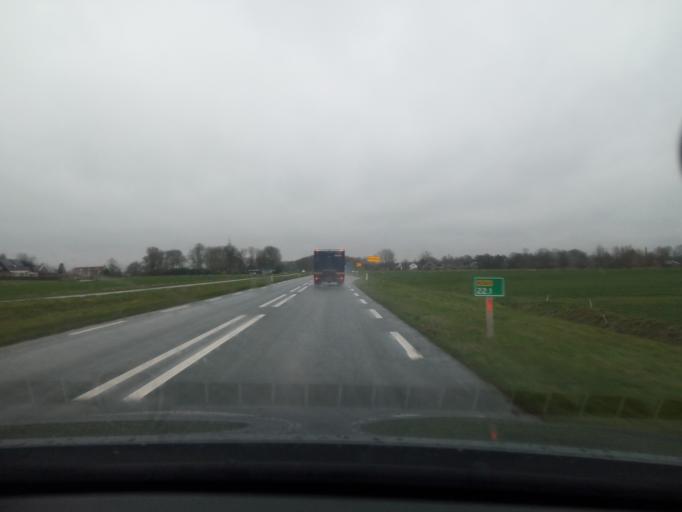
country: NL
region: Groningen
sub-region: Gemeente Appingedam
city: Appingedam
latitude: 53.3224
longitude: 6.8271
